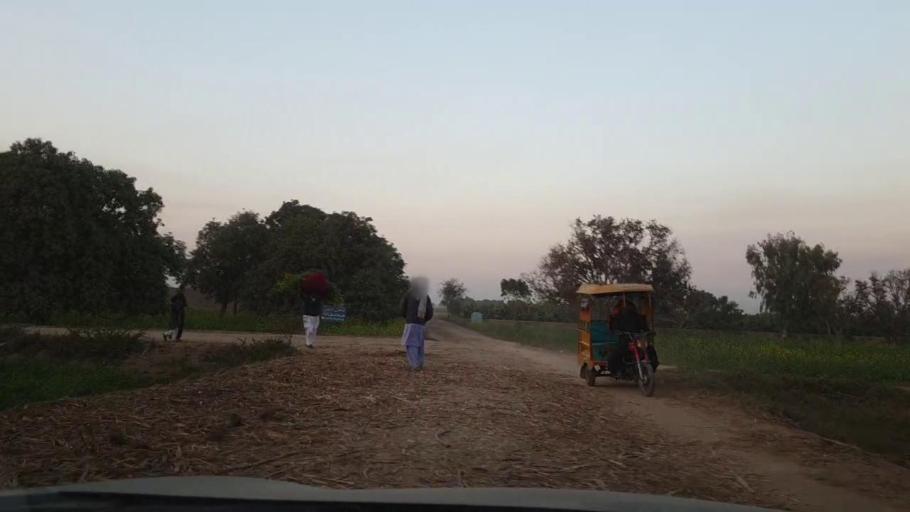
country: PK
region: Sindh
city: Berani
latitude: 25.6643
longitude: 68.7885
